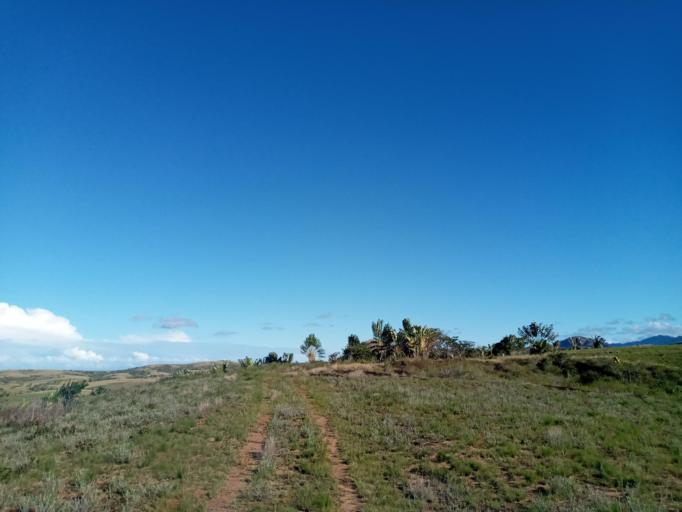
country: MG
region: Anosy
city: Fort Dauphin
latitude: -24.4069
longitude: 47.2547
